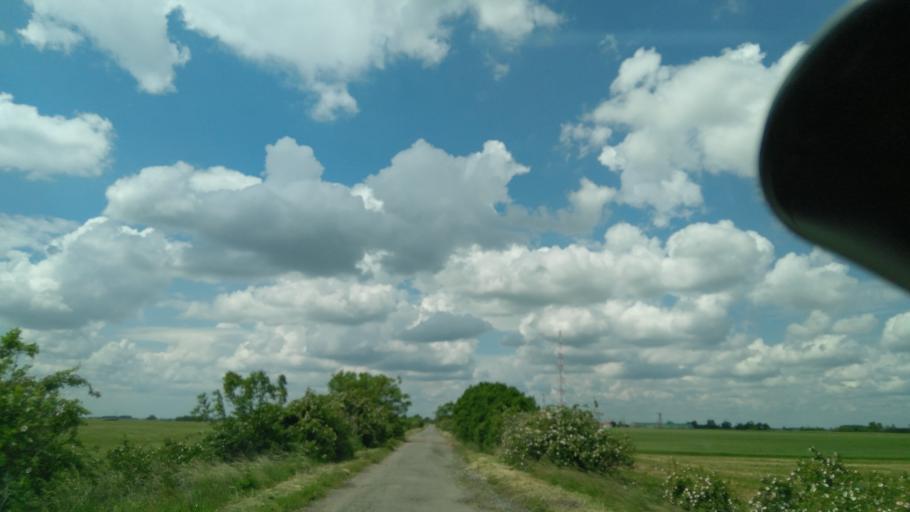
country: HU
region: Bekes
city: Devavanya
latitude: 47.0227
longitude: 20.9359
